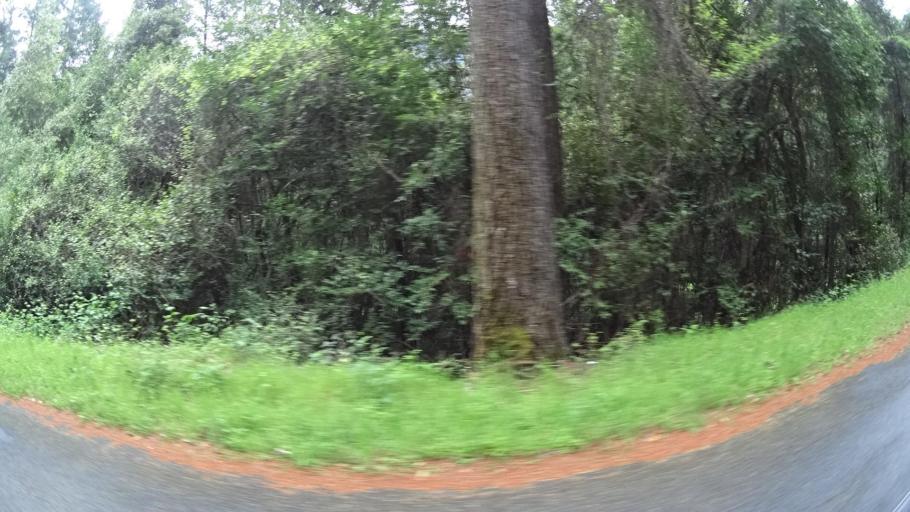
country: US
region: California
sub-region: Humboldt County
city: Willow Creek
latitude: 41.3333
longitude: -123.5211
